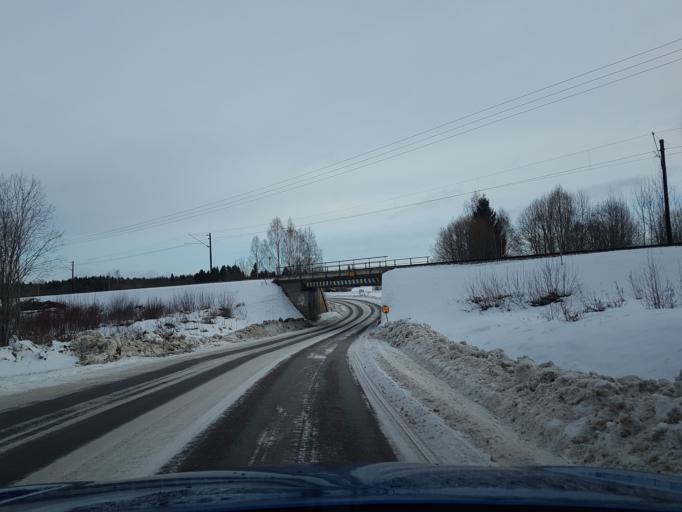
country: SE
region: Dalarna
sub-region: Leksand Municipality
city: Leksand
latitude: 60.7570
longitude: 15.0172
